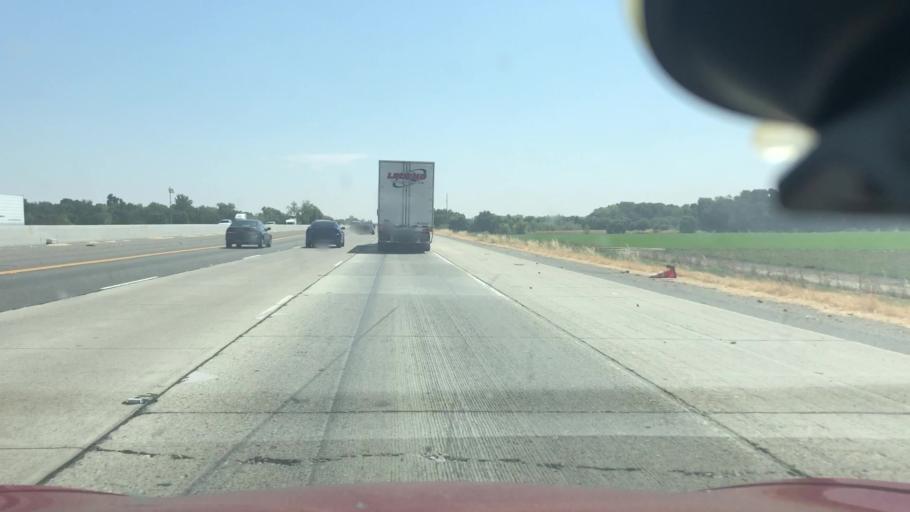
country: US
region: California
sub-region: Sacramento County
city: Parkway
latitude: 38.4447
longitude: -121.4915
